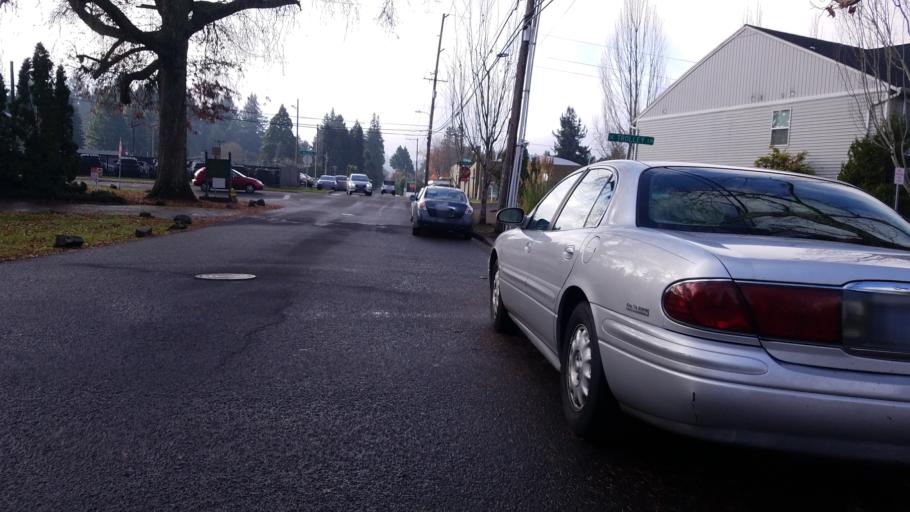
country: US
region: Oregon
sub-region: Clackamas County
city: Jennings Lodge
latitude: 45.3899
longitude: -122.6093
